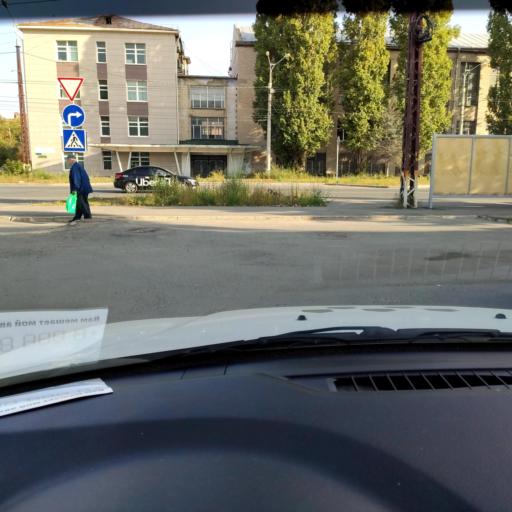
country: RU
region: Samara
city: Tol'yatti
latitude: 53.5201
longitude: 49.4305
